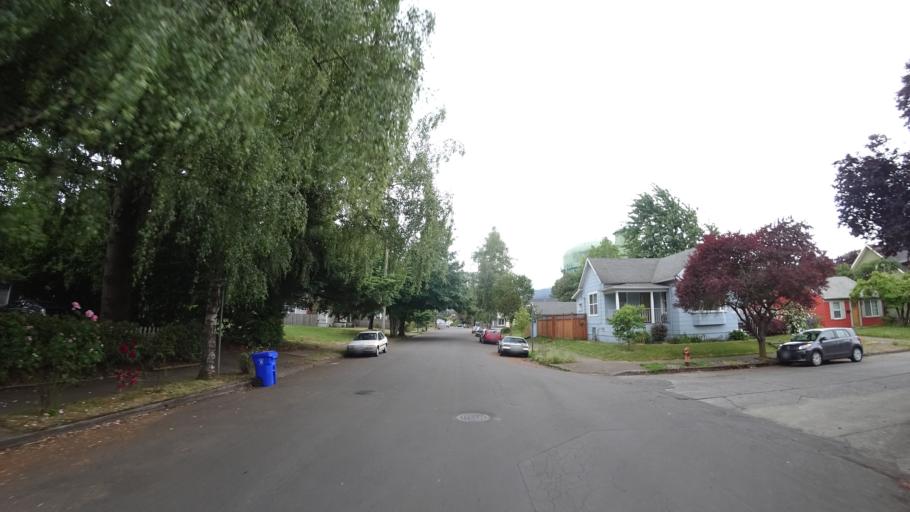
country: US
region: Oregon
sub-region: Washington County
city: West Haven
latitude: 45.5873
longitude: -122.7499
